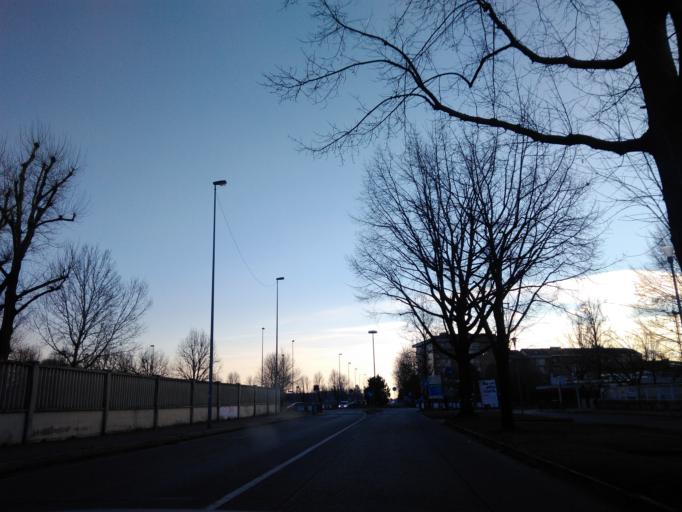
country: IT
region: Piedmont
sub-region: Provincia di Torino
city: Grugliasco
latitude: 45.0654
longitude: 7.5884
